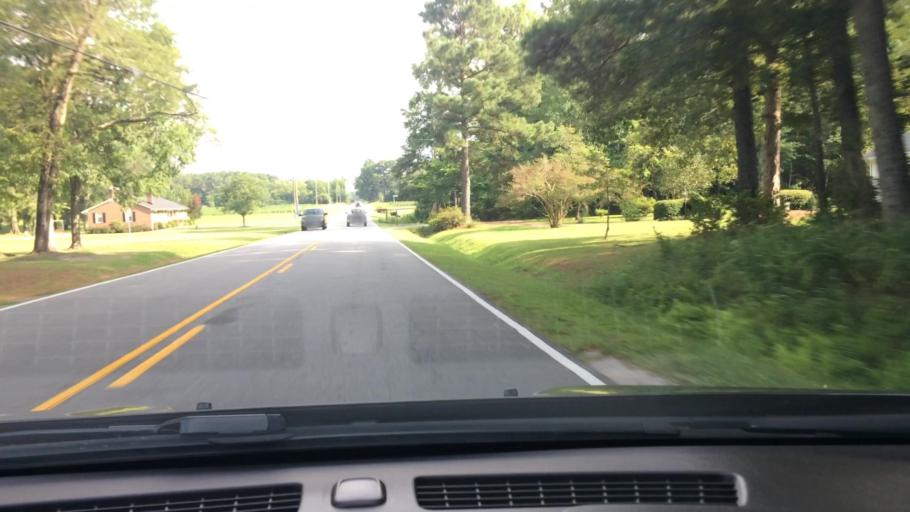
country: US
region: North Carolina
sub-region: Pitt County
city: Winterville
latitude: 35.5024
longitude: -77.3803
